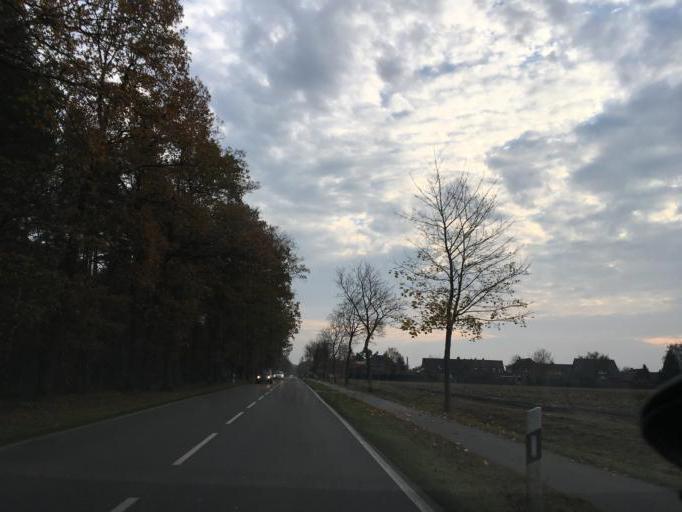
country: DE
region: Lower Saxony
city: Wietzendorf
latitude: 52.9331
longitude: 9.9811
